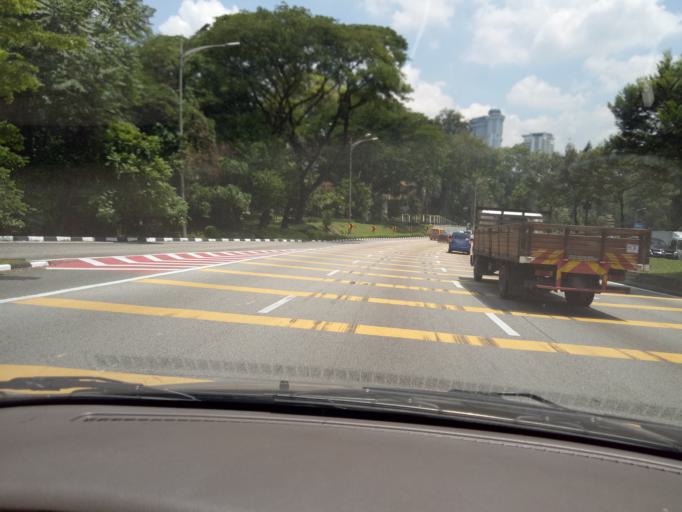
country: MY
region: Kuala Lumpur
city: Kuala Lumpur
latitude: 3.1324
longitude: 101.6992
